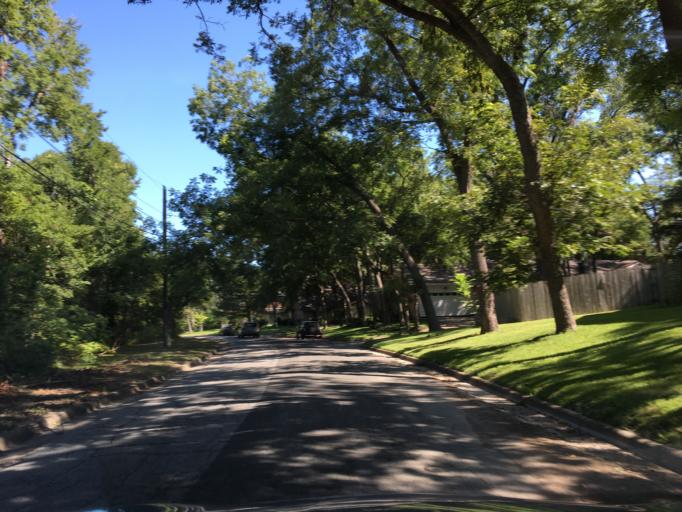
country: US
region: Texas
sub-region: Dallas County
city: Garland
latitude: 32.8590
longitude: -96.7001
